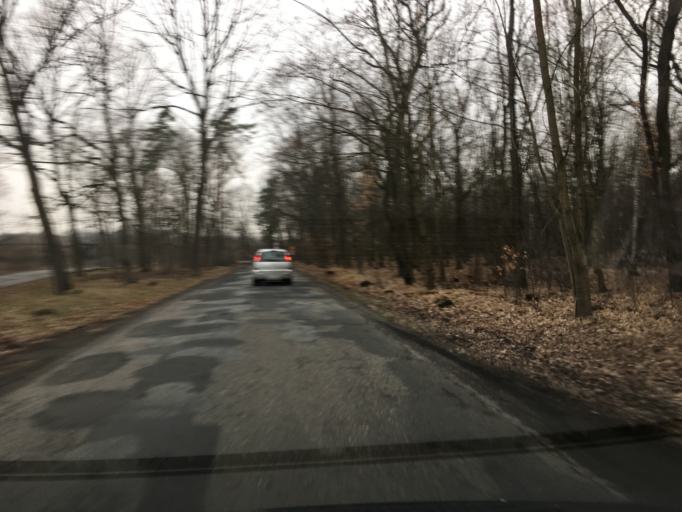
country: PL
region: Opole Voivodeship
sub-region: Powiat kedzierzynsko-kozielski
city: Kedzierzyn-Kozle
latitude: 50.3222
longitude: 18.2317
